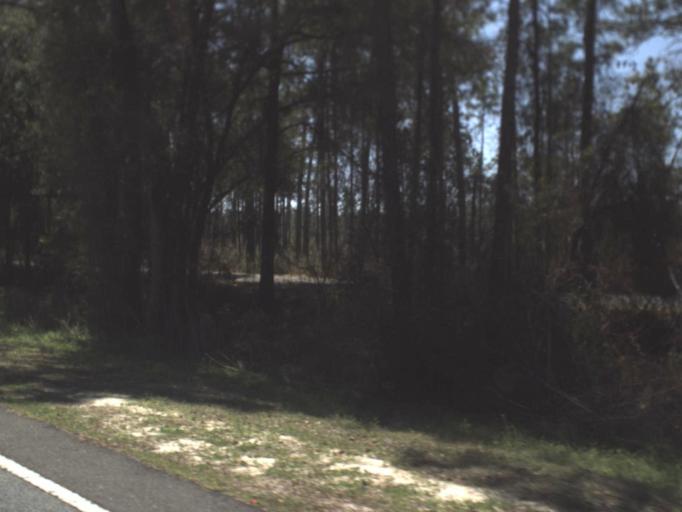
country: US
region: Florida
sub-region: Leon County
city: Woodville
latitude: 30.3472
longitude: -84.2577
